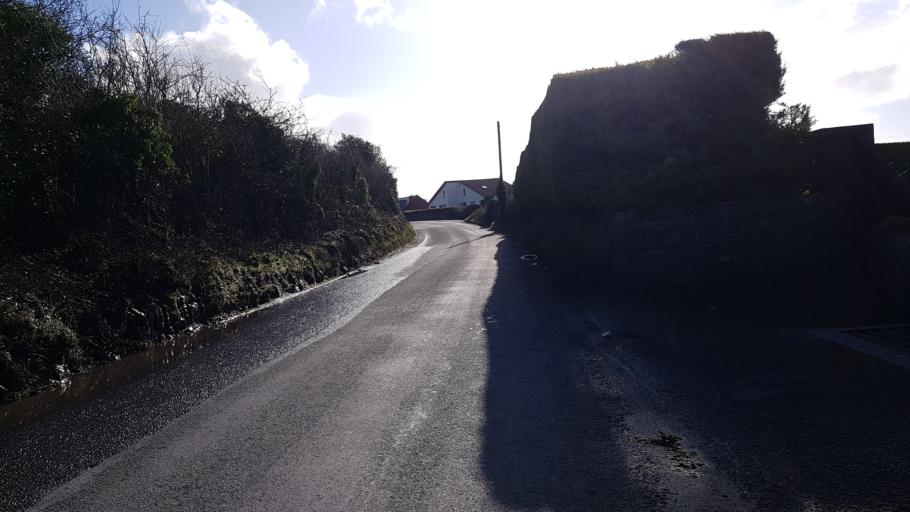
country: IE
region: Connaught
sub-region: County Galway
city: Gaillimh
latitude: 53.3047
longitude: -9.0199
